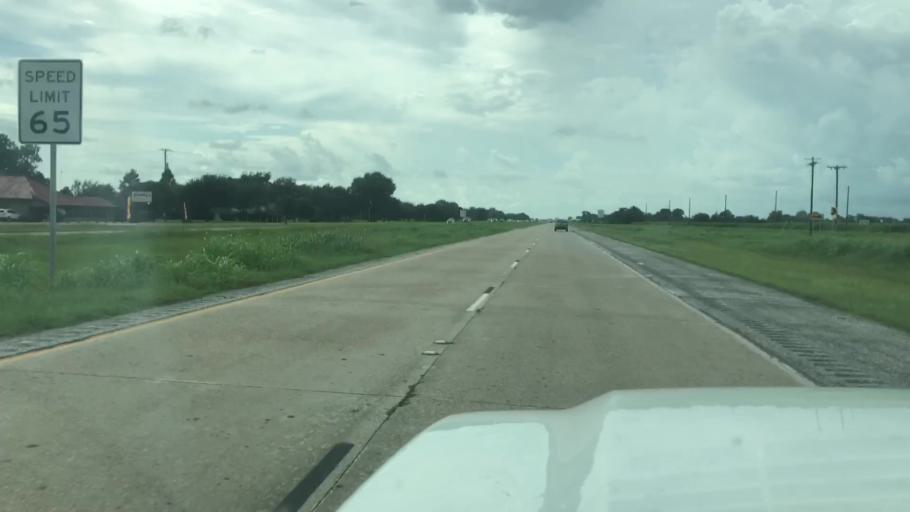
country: US
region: Louisiana
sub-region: Iberia Parish
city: Jeanerette
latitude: 29.8728
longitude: -91.6458
